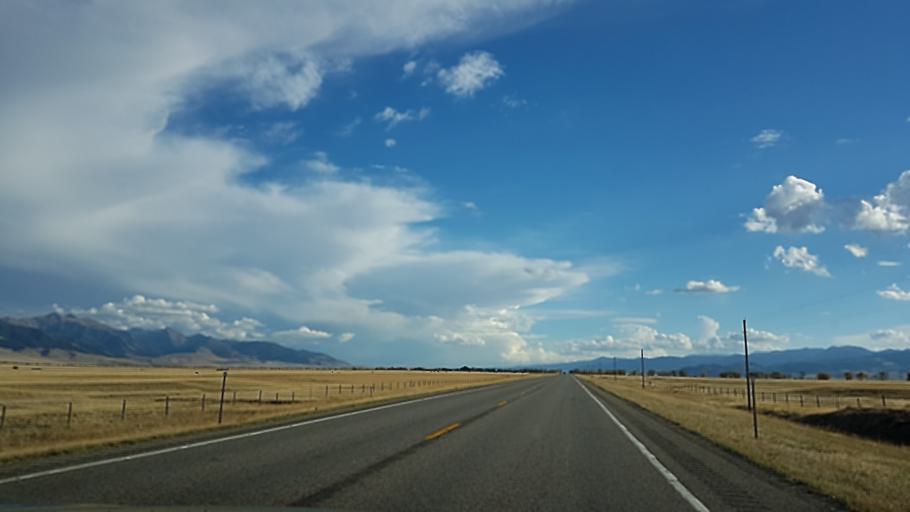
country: US
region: Montana
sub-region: Madison County
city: Virginia City
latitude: 45.2264
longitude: -111.6789
